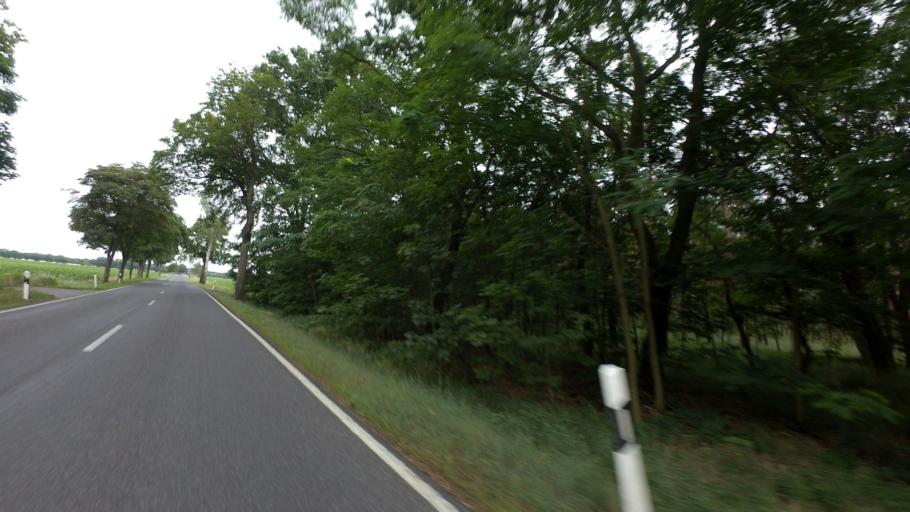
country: DE
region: Brandenburg
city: Crinitz
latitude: 51.8017
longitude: 13.8341
